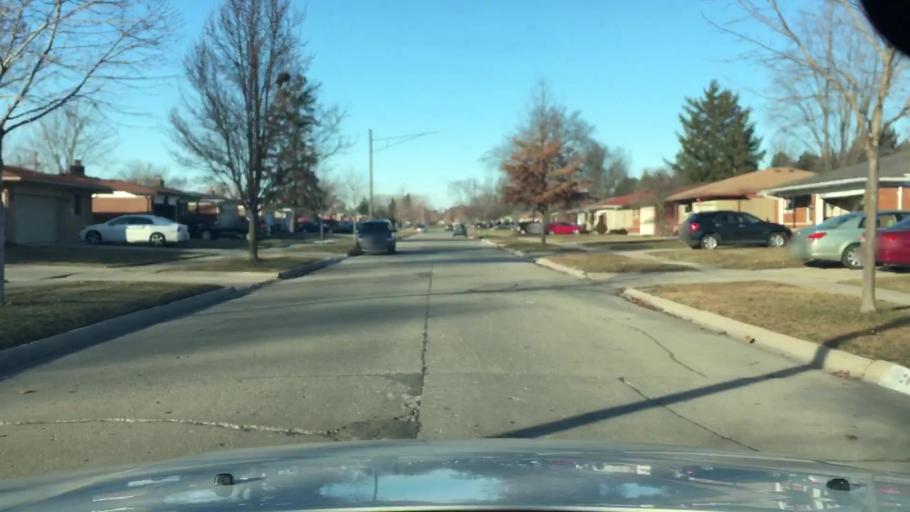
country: US
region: Michigan
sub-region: Oakland County
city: Madison Heights
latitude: 42.4998
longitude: -83.0772
